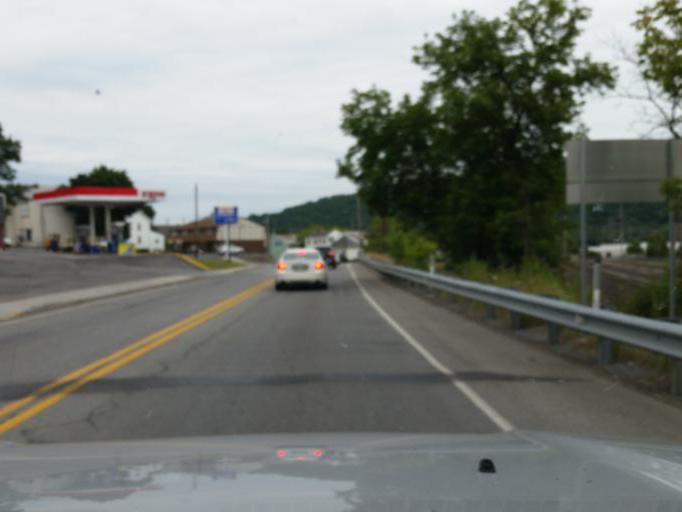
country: US
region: Pennsylvania
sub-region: Blair County
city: Hollidaysburg
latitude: 40.4275
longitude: -78.3961
